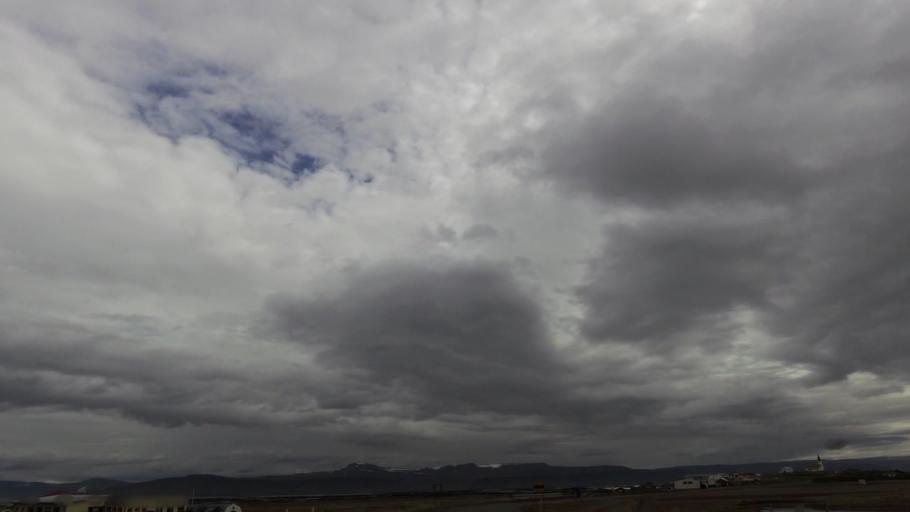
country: IS
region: West
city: Stykkisholmur
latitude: 65.4550
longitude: -22.2013
